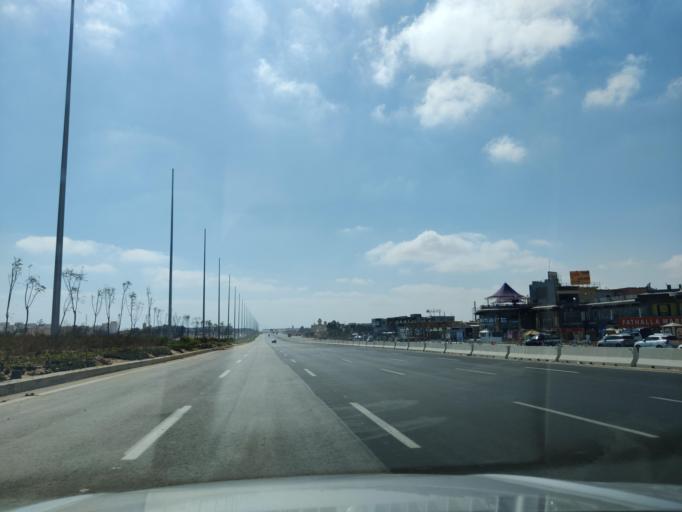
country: EG
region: Muhafazat Matruh
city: Al `Alamayn
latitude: 30.9913
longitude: 28.6787
